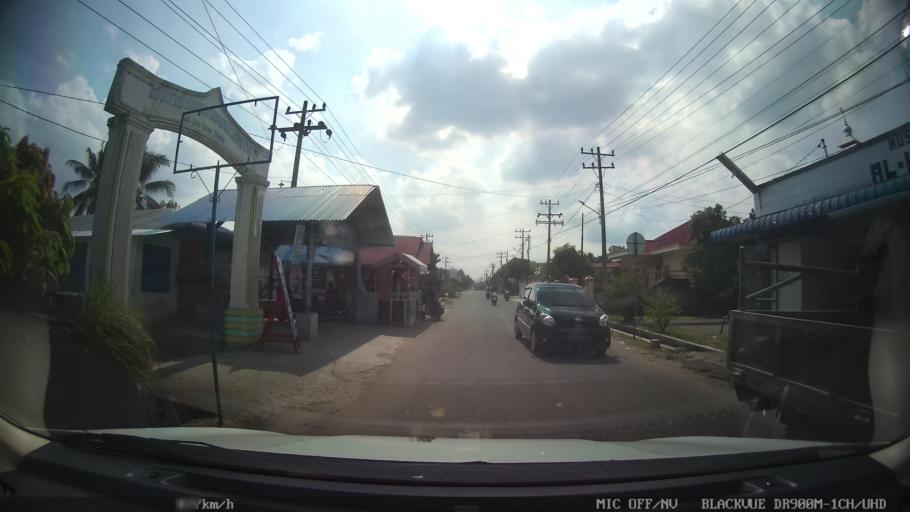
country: ID
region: North Sumatra
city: Binjai
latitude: 3.6438
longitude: 98.5066
